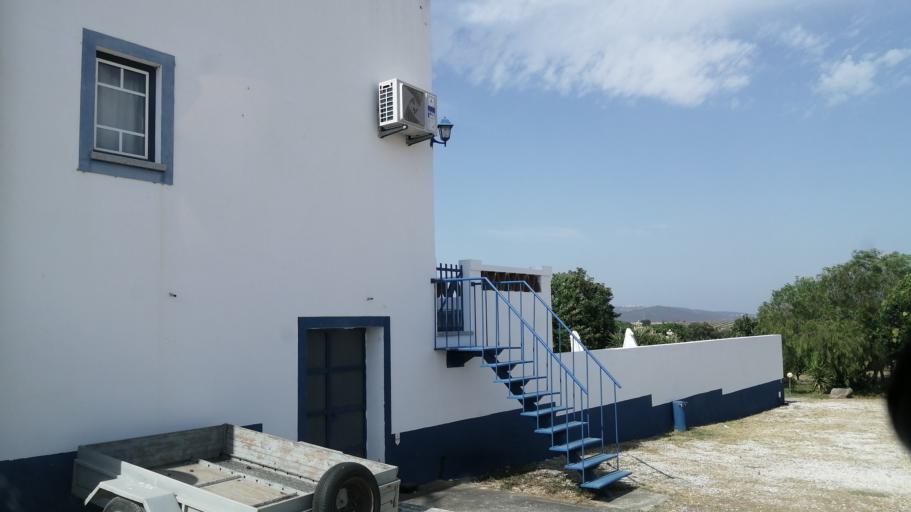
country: PT
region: Evora
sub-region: Mourao
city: Mourao
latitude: 38.3947
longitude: -7.3188
